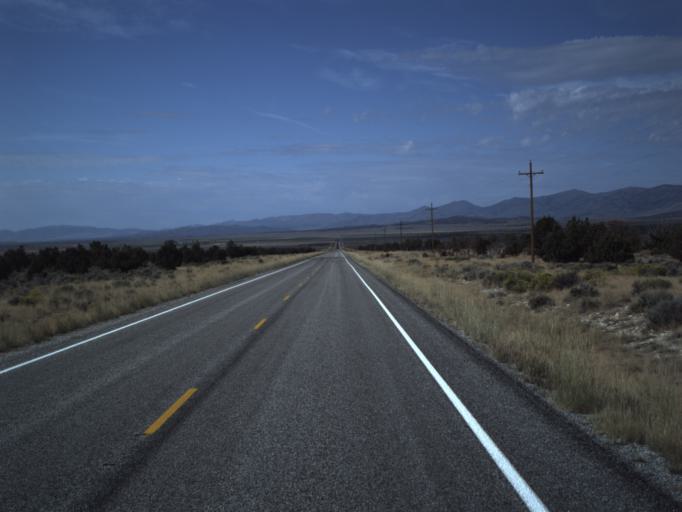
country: US
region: Idaho
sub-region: Cassia County
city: Burley
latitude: 41.8061
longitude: -113.4494
